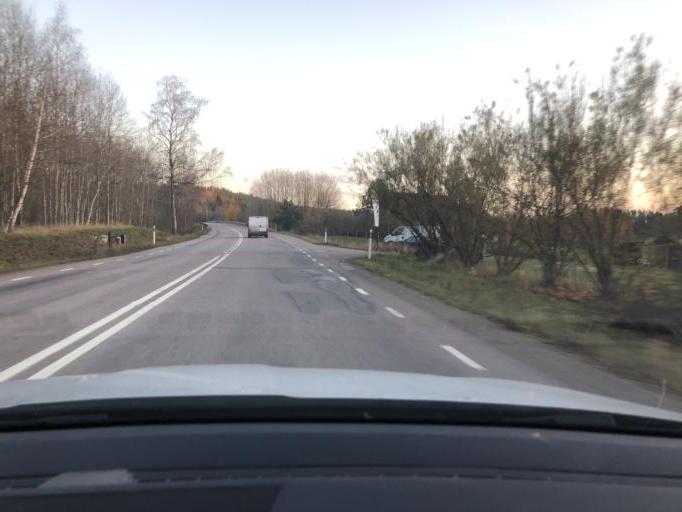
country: SE
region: Soedermanland
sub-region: Strangnas Kommun
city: Akers Styckebruk
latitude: 59.3096
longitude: 17.0858
